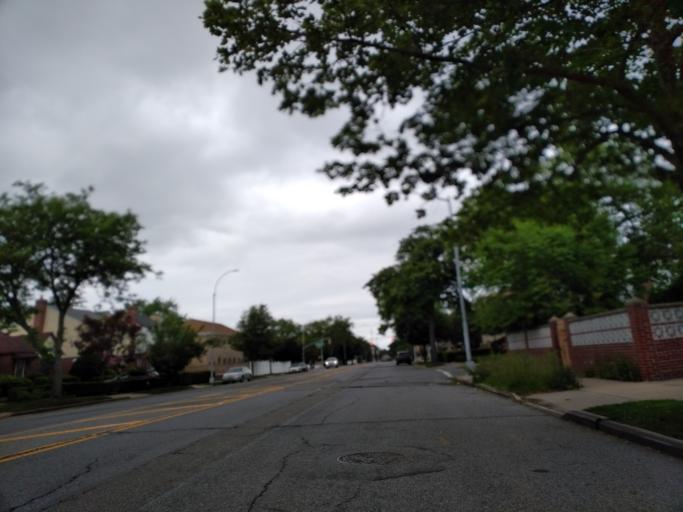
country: US
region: New York
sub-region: Nassau County
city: East Atlantic Beach
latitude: 40.7727
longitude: -73.7924
